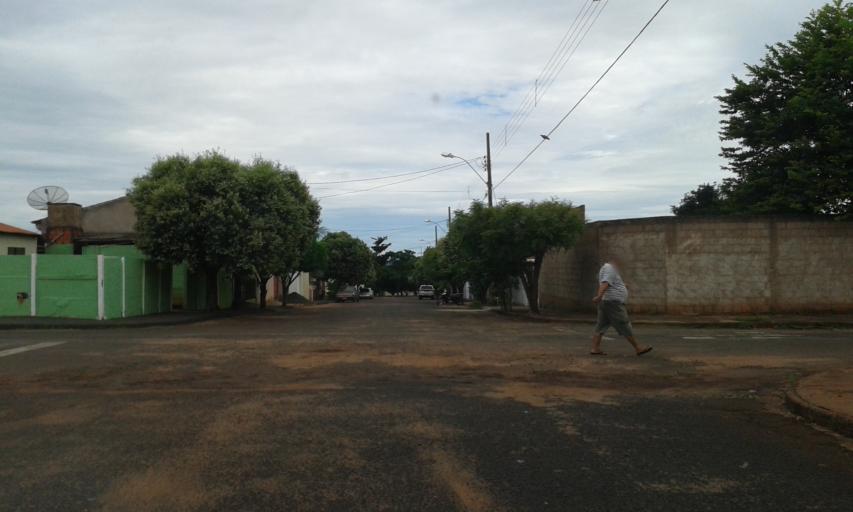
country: BR
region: Minas Gerais
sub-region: Ituiutaba
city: Ituiutaba
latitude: -18.9815
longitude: -49.4494
